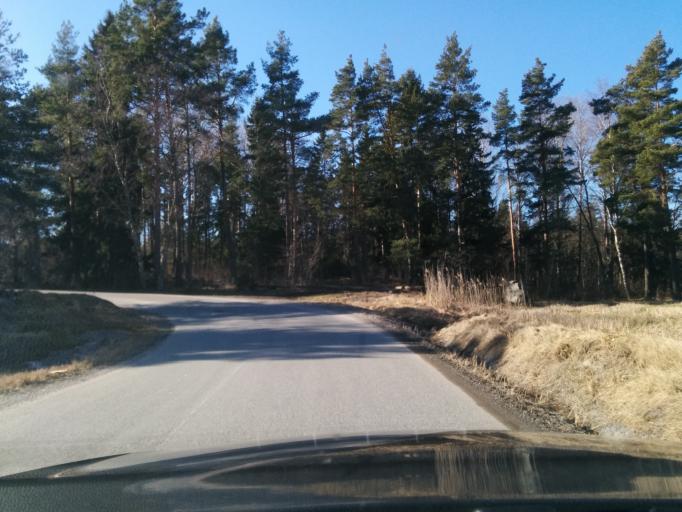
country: SE
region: Stockholm
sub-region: Vallentuna Kommun
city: Vallentuna
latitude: 59.5223
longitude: 18.0342
